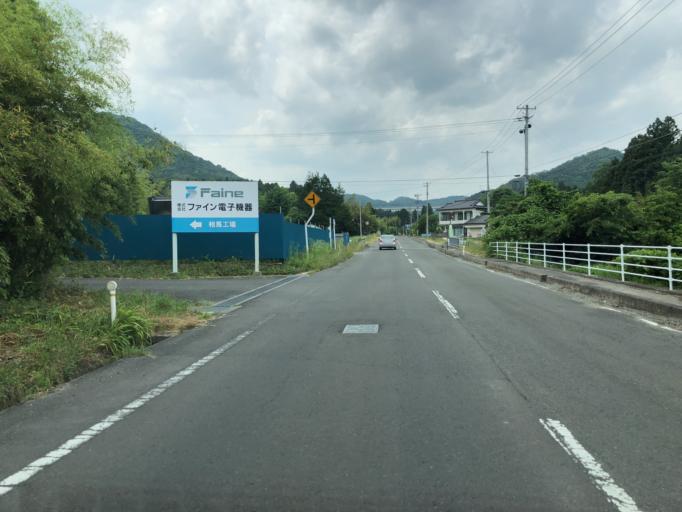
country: JP
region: Miyagi
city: Marumori
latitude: 37.8216
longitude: 140.8821
